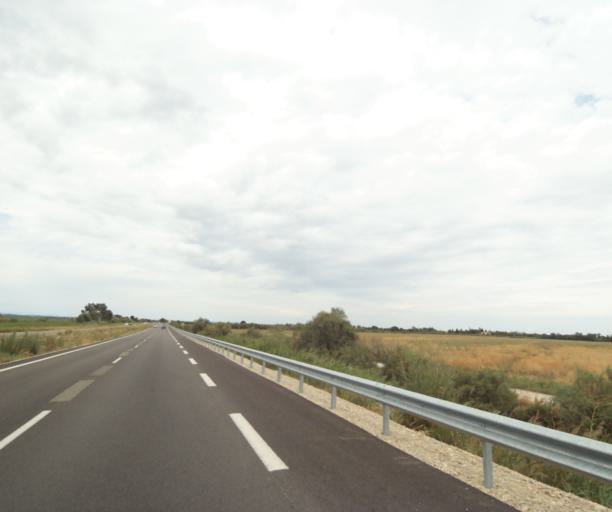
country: FR
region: Languedoc-Roussillon
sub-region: Departement de l'Herault
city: La Grande-Motte
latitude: 43.5898
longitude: 4.1048
